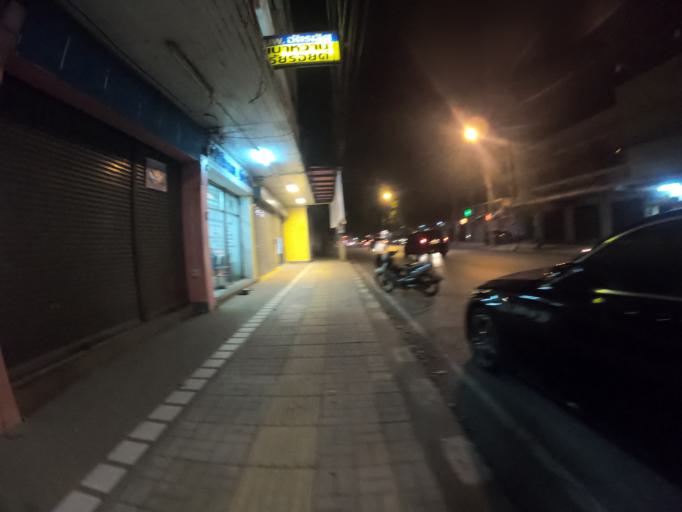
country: TH
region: Khon Kaen
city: Khon Kaen
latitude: 16.4333
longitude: 102.8343
